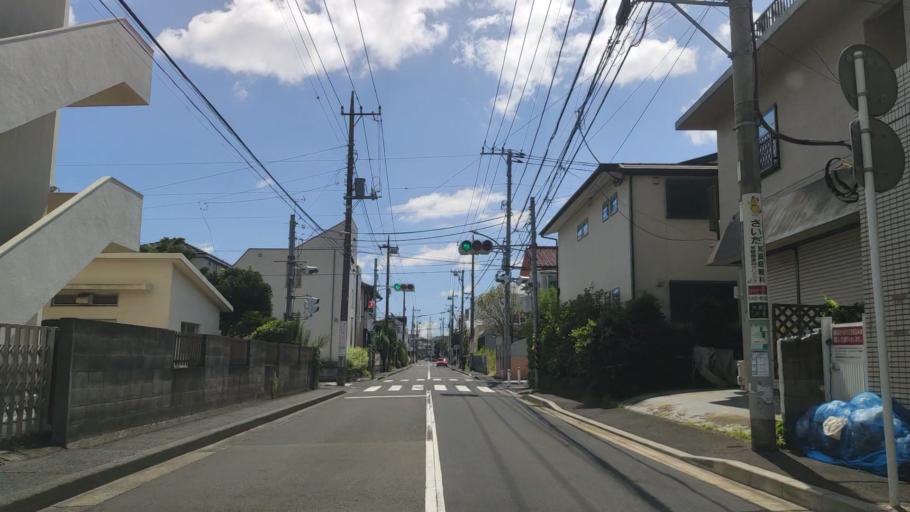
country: JP
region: Kanagawa
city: Yokohama
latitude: 35.5204
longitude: 139.6249
